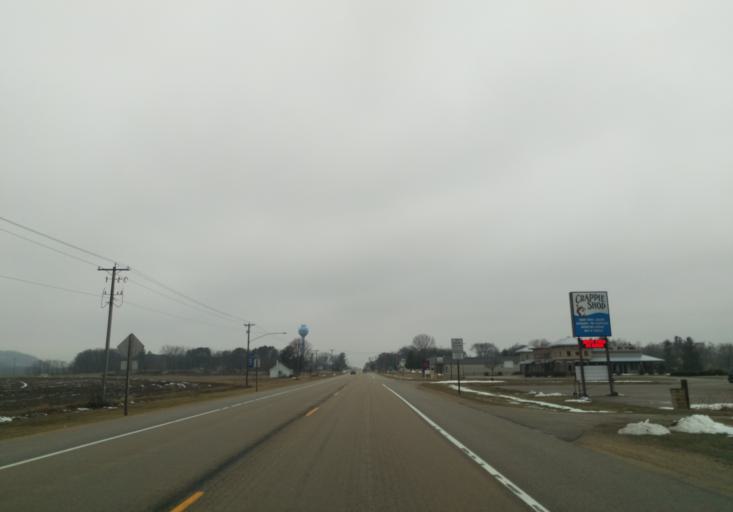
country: US
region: Wisconsin
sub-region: Dane County
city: Mazomanie
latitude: 43.1617
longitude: -89.8979
